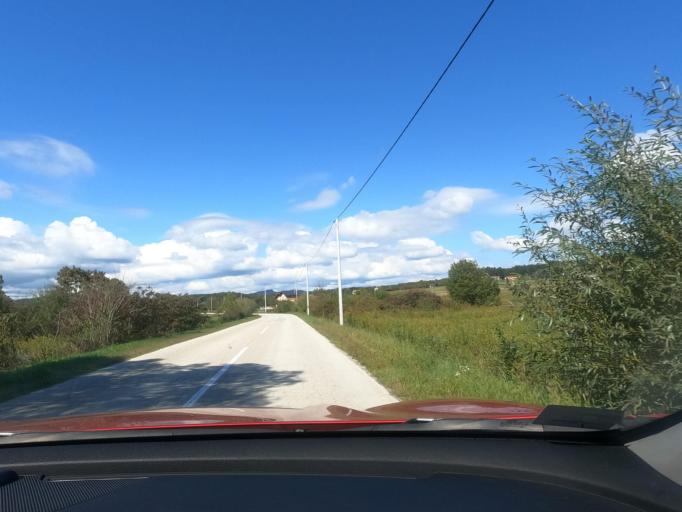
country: BA
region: Federation of Bosnia and Herzegovina
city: Podzvizd
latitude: 45.2275
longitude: 15.9060
